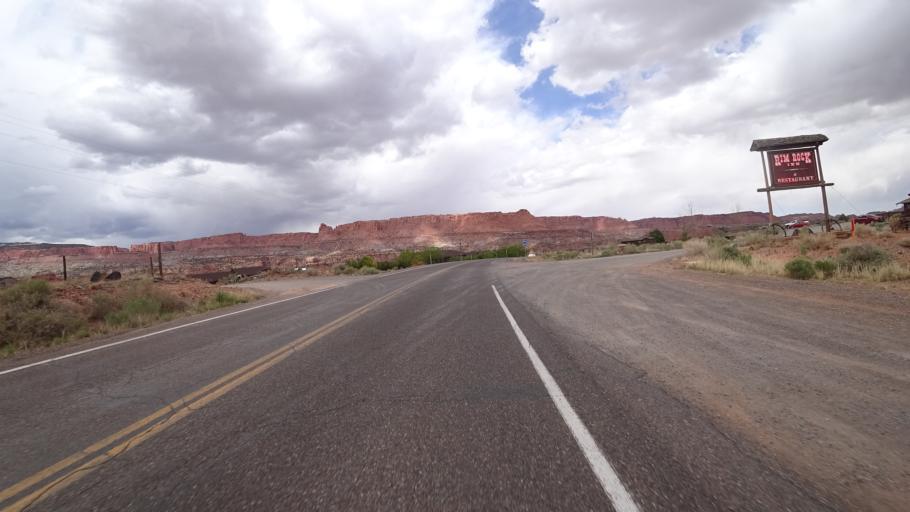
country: US
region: Utah
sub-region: Wayne County
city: Loa
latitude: 38.3187
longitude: -111.3839
